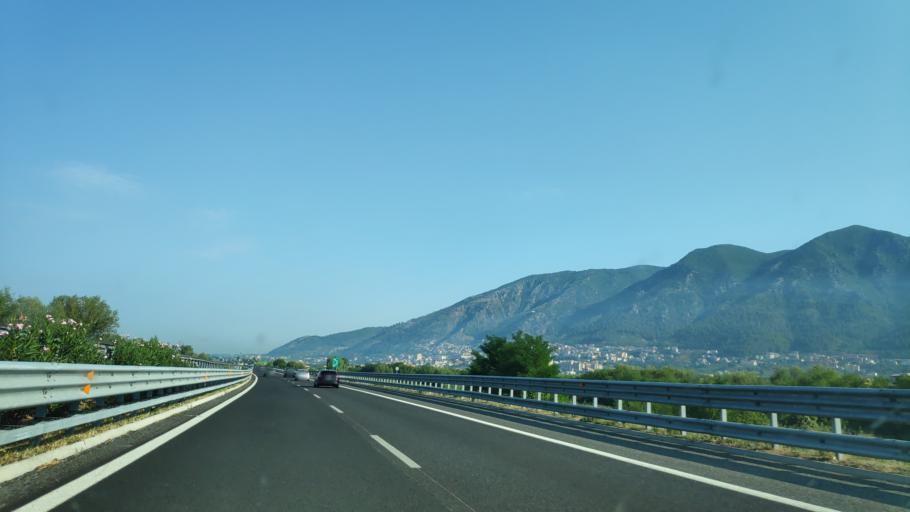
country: IT
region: Campania
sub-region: Provincia di Salerno
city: Sala Consilina
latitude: 40.3743
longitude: 15.5992
